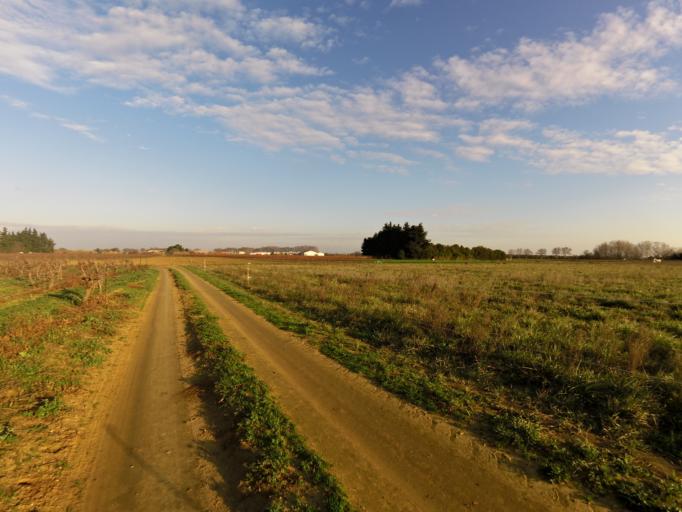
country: FR
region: Languedoc-Roussillon
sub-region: Departement du Gard
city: Gallargues-le-Montueux
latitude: 43.7129
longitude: 4.1904
